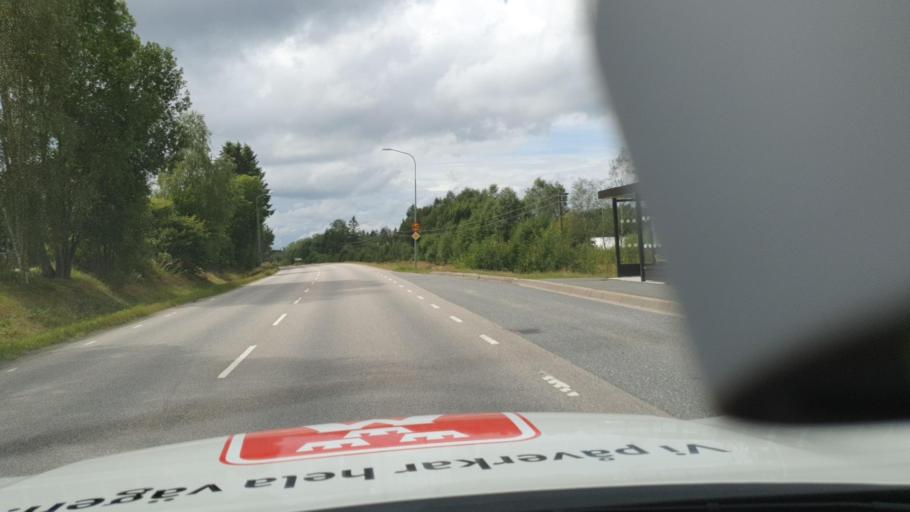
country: SE
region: Vaestra Goetaland
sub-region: Harryda Kommun
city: Hindas
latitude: 57.7035
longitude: 12.4377
